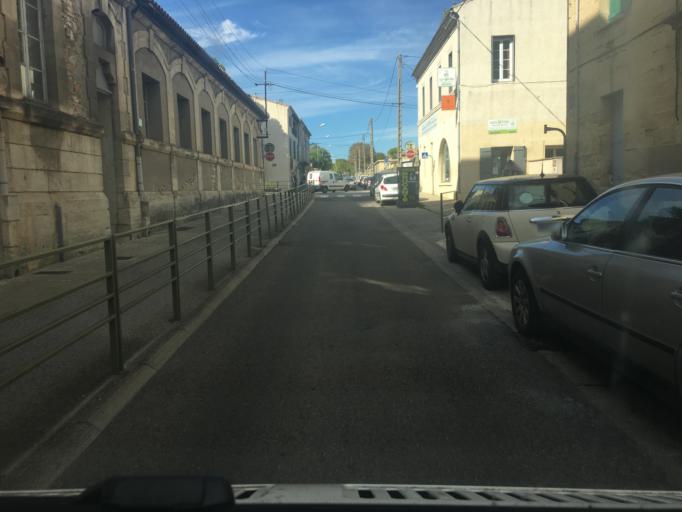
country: FR
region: Languedoc-Roussillon
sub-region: Departement du Gard
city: Uzes
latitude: 44.0149
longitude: 4.4174
